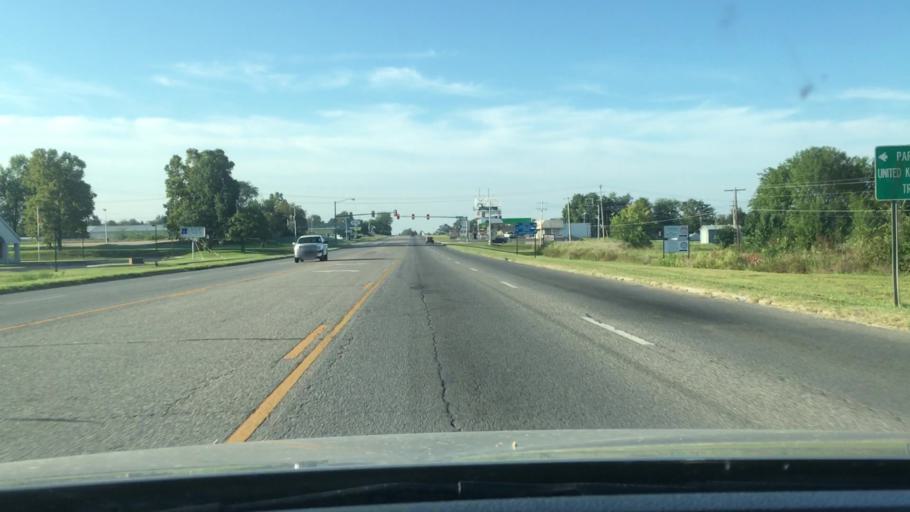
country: US
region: Oklahoma
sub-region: Cherokee County
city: Park Hill
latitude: 35.8727
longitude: -94.9763
